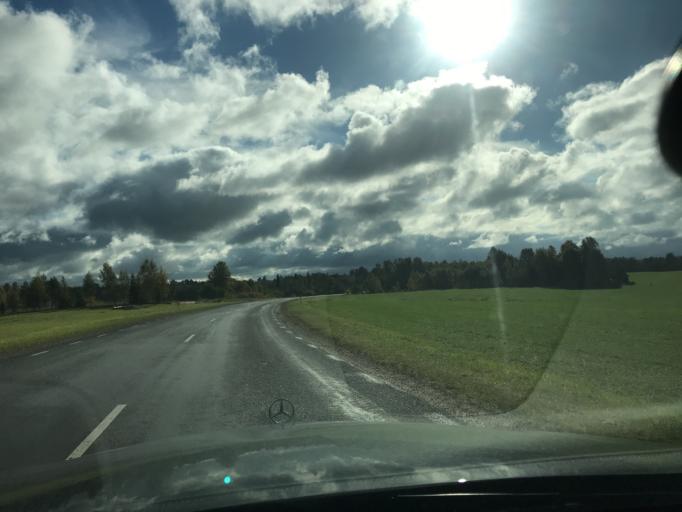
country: EE
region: Tartu
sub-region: Elva linn
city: Elva
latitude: 58.0064
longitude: 26.2621
